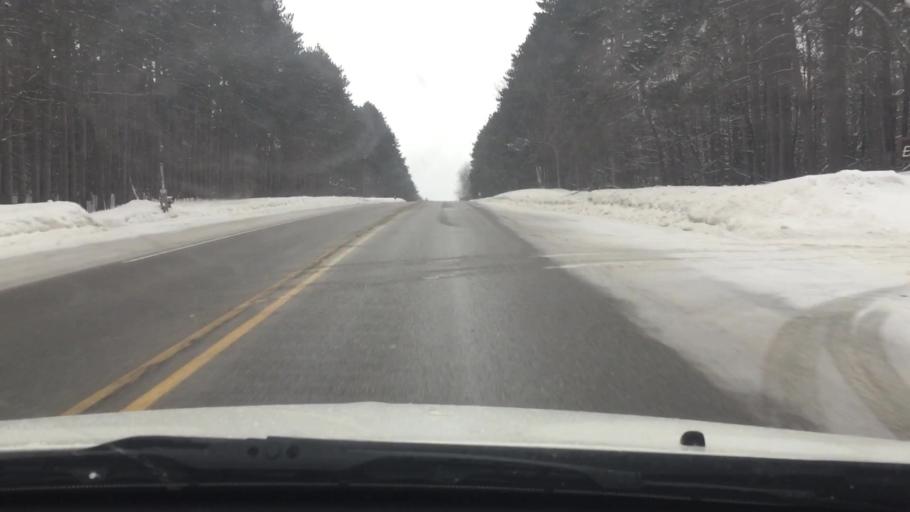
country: US
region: Michigan
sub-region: Otsego County
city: Gaylord
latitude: 45.0618
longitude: -84.8074
